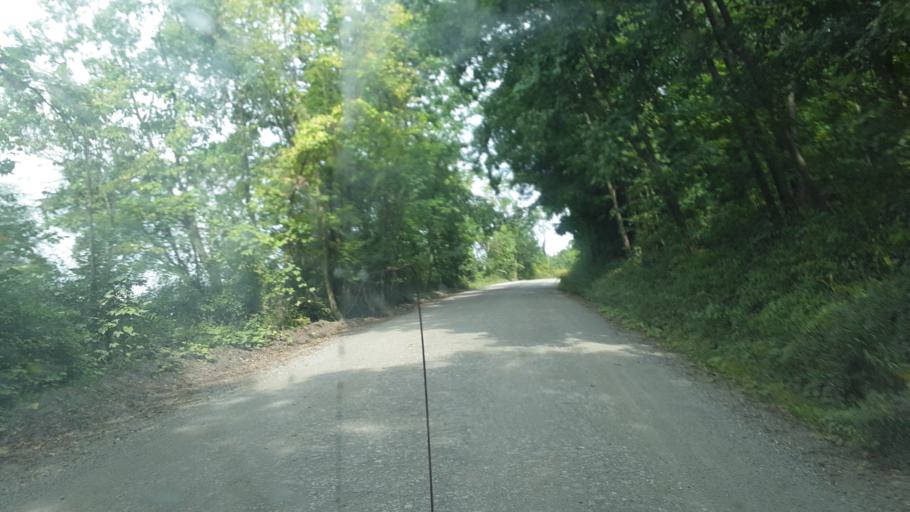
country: US
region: Pennsylvania
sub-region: Jefferson County
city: Punxsutawney
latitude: 40.9293
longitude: -79.0529
